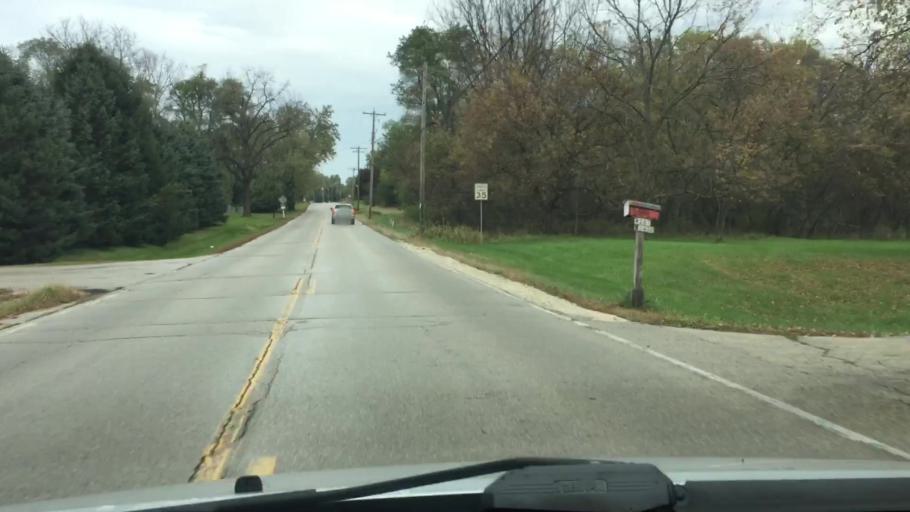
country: US
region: Wisconsin
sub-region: Waukesha County
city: Pewaukee
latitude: 43.0648
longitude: -88.2795
